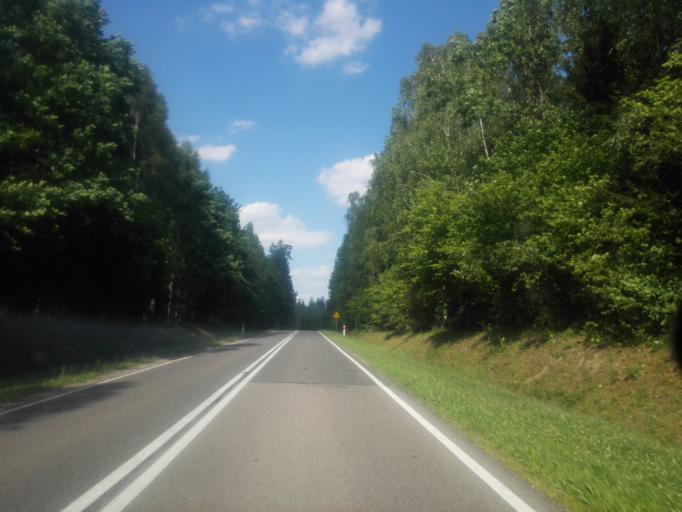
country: PL
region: Podlasie
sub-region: Powiat sejnenski
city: Sejny
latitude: 54.0065
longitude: 23.3220
